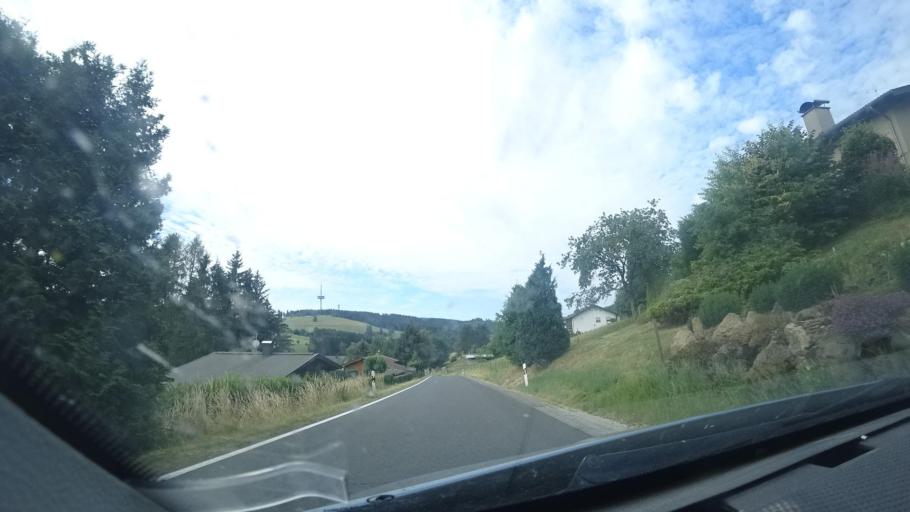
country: DE
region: Rheinland-Pfalz
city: Hohenleimbach
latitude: 50.4450
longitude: 7.0806
